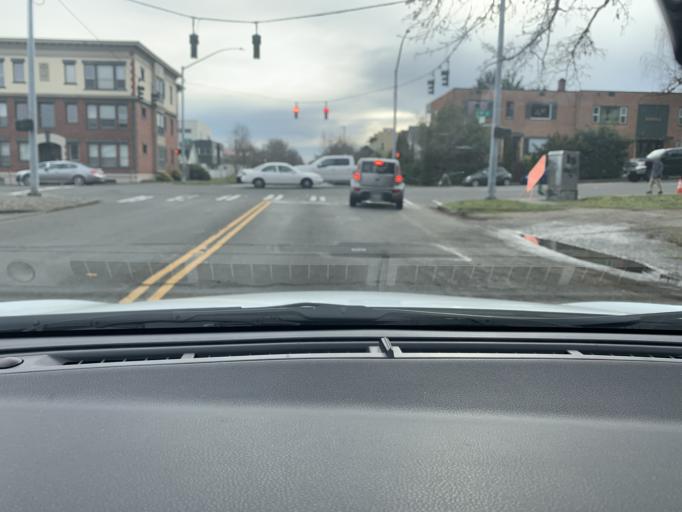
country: US
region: Washington
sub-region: Pierce County
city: Tacoma
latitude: 47.2546
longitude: -122.4509
